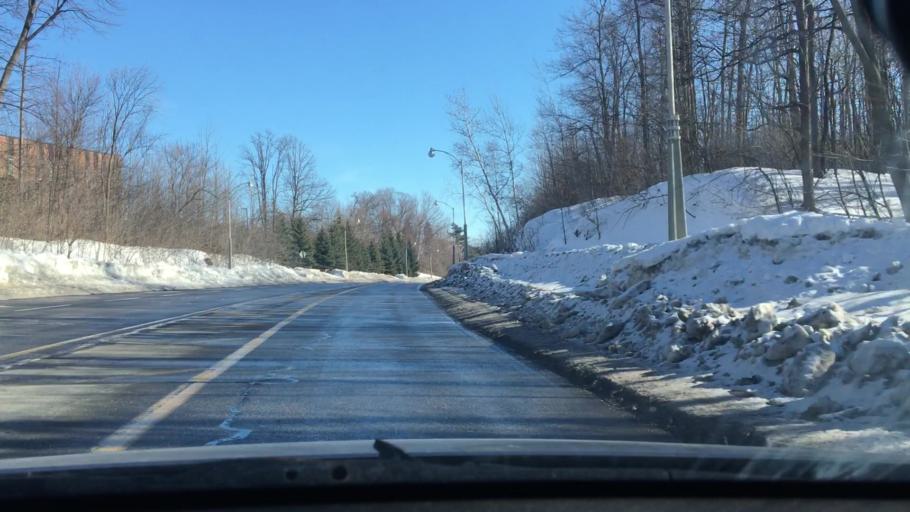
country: CA
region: Ontario
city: Ottawa
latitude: 45.4457
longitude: -75.6412
